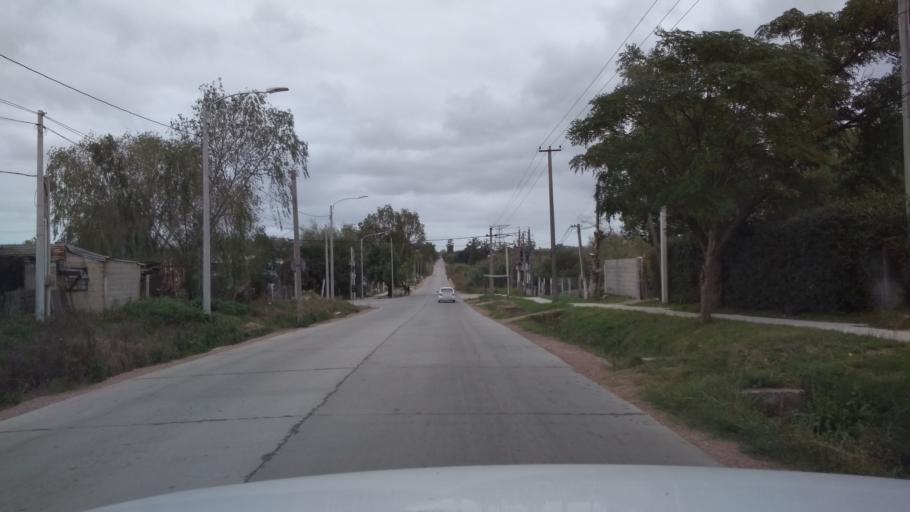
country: UY
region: Canelones
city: Toledo
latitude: -34.7893
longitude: -56.1447
